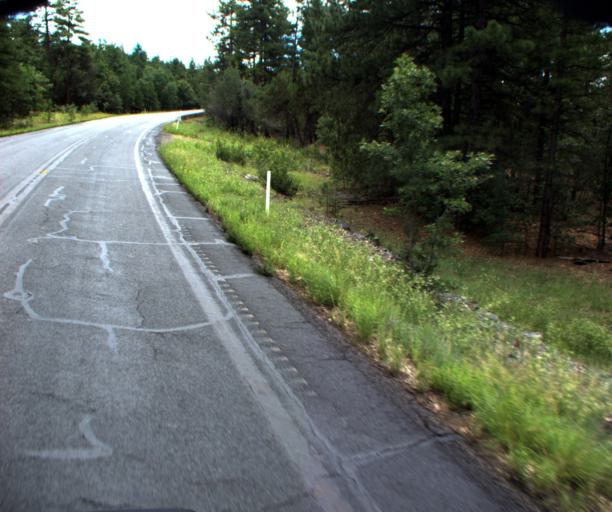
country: US
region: Arizona
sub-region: Gila County
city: Pine
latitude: 34.5204
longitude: -111.5078
